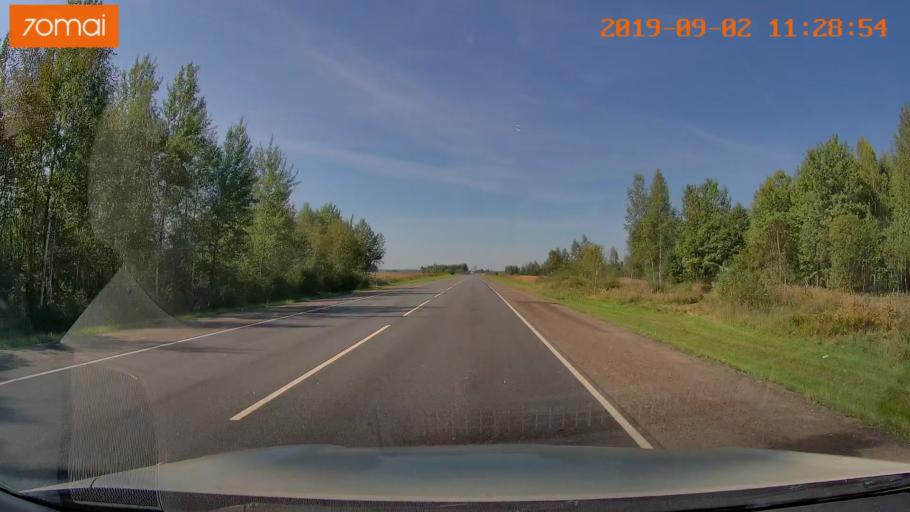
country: RU
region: Smolensk
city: Roslavl'
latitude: 53.9920
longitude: 32.8745
